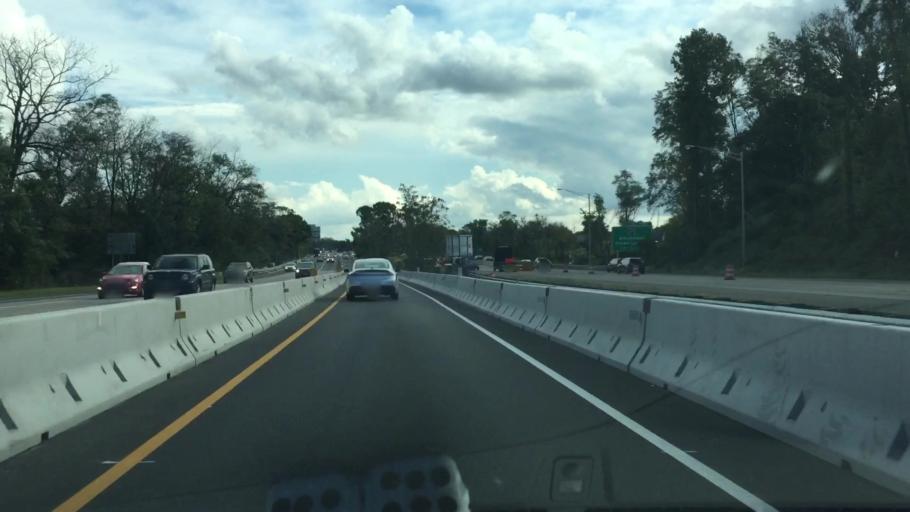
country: US
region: New Jersey
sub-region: Camden County
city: Glendora
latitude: 39.8277
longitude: -75.0857
